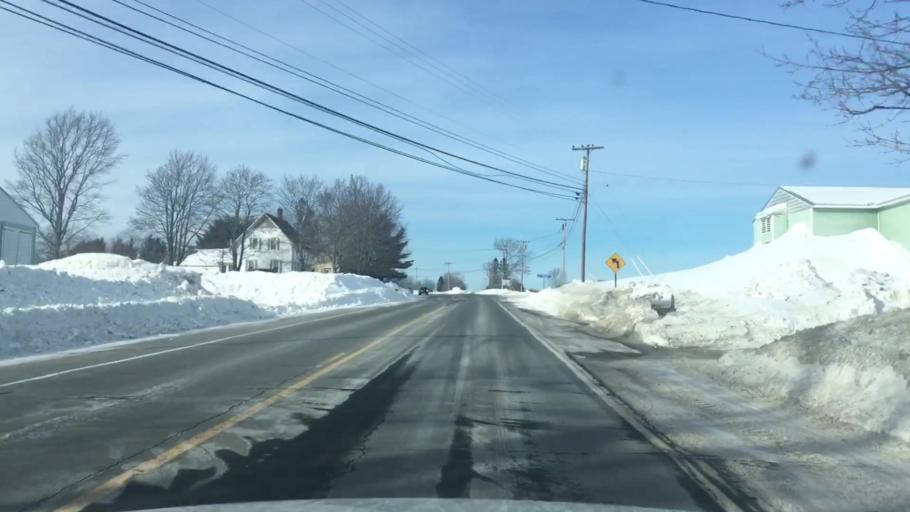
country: US
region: Maine
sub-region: Penobscot County
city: Charleston
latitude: 45.0258
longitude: -69.0302
